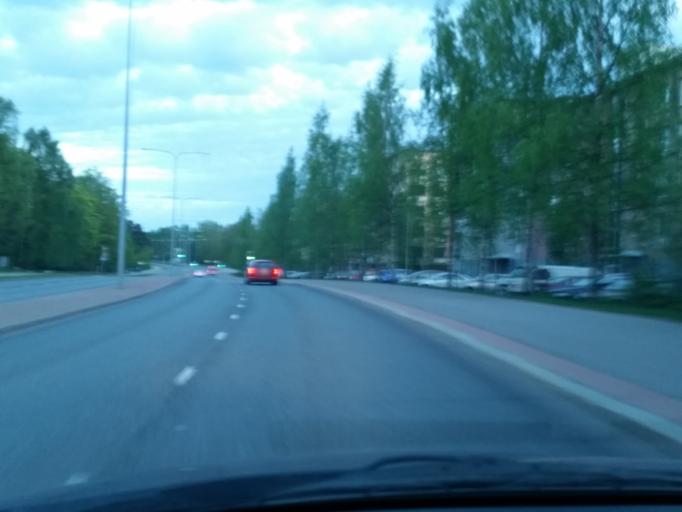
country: FI
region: Uusimaa
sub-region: Helsinki
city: Vantaa
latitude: 60.1906
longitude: 25.0396
